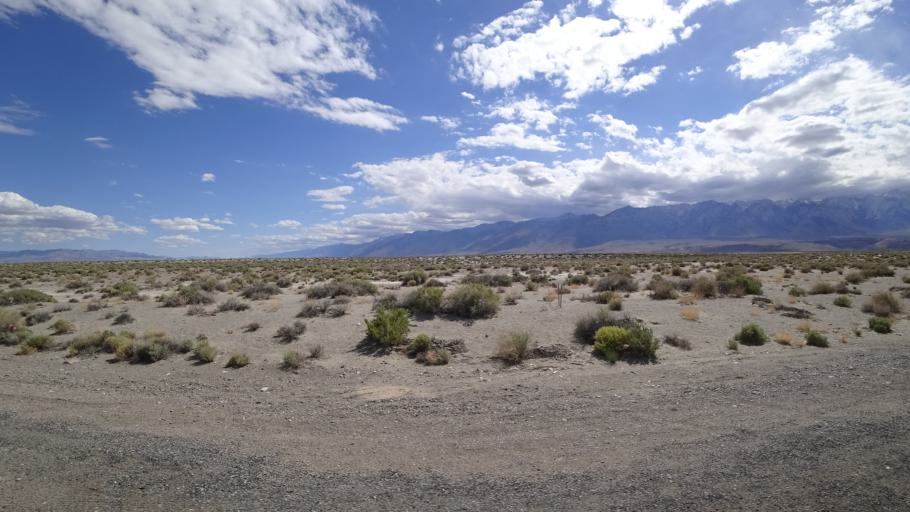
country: US
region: California
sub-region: Inyo County
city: Lone Pine
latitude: 36.5599
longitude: -117.9679
